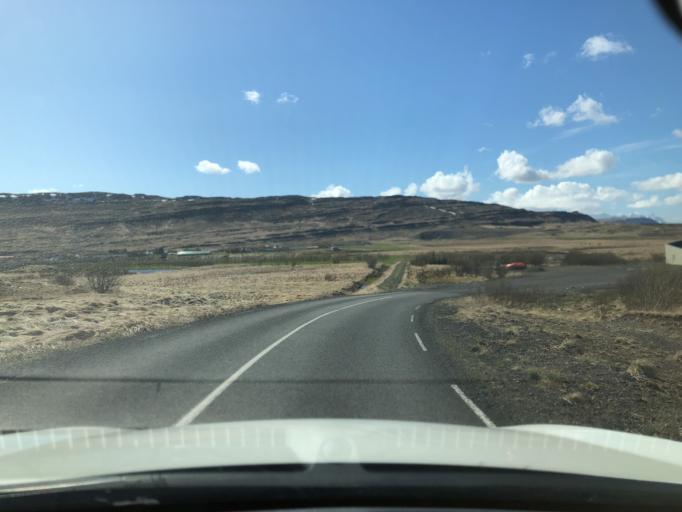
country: IS
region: West
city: Borgarnes
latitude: 64.6641
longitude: -21.4070
